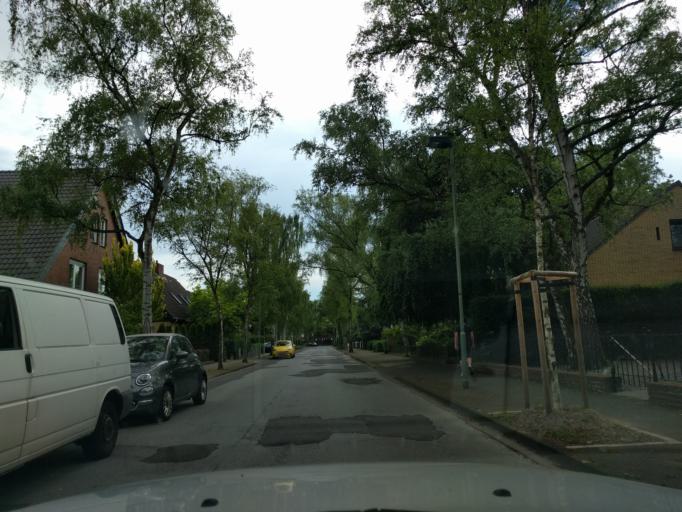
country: DE
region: North Rhine-Westphalia
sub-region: Regierungsbezirk Dusseldorf
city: Meerbusch
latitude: 51.2516
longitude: 6.7031
